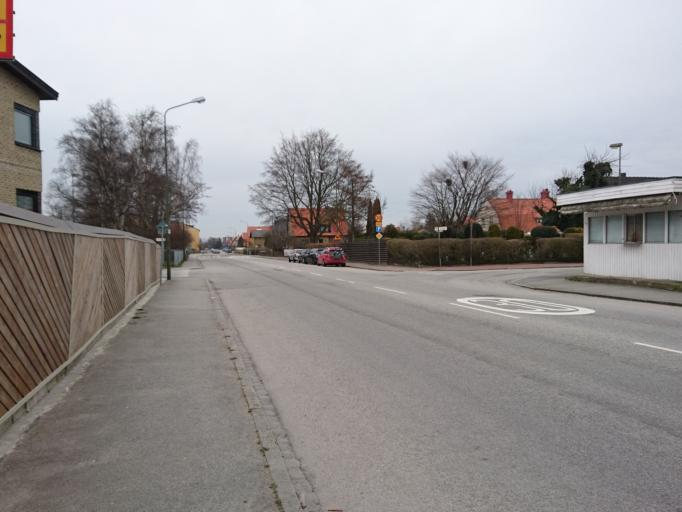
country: SE
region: Skane
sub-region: Malmo
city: Malmoe
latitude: 55.5760
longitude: 13.0349
